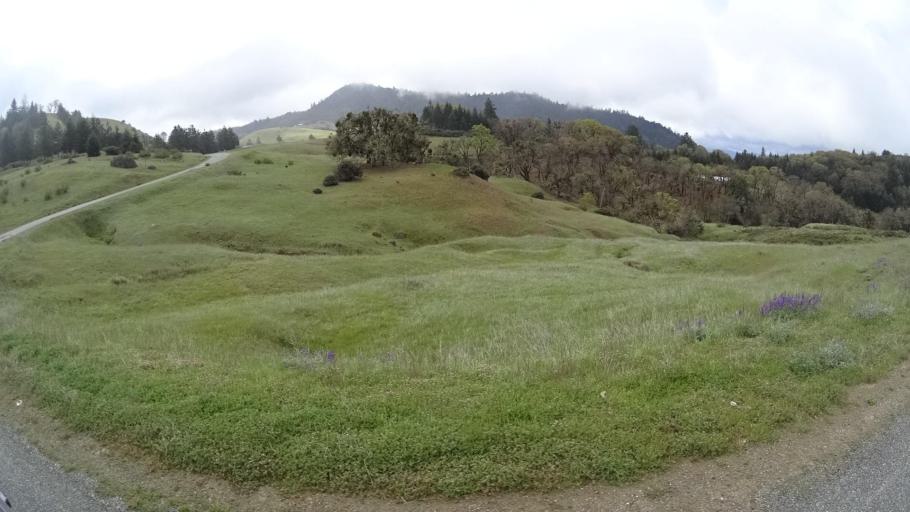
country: US
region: California
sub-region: Humboldt County
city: Redway
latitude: 40.1562
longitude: -123.5426
